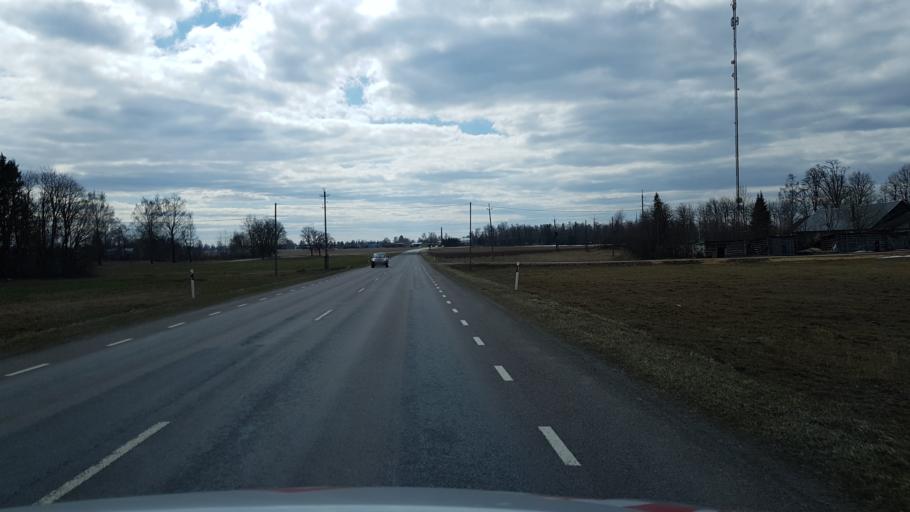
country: EE
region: Laeaene-Virumaa
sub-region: Vaeike-Maarja vald
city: Vaike-Maarja
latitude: 59.1410
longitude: 26.2610
